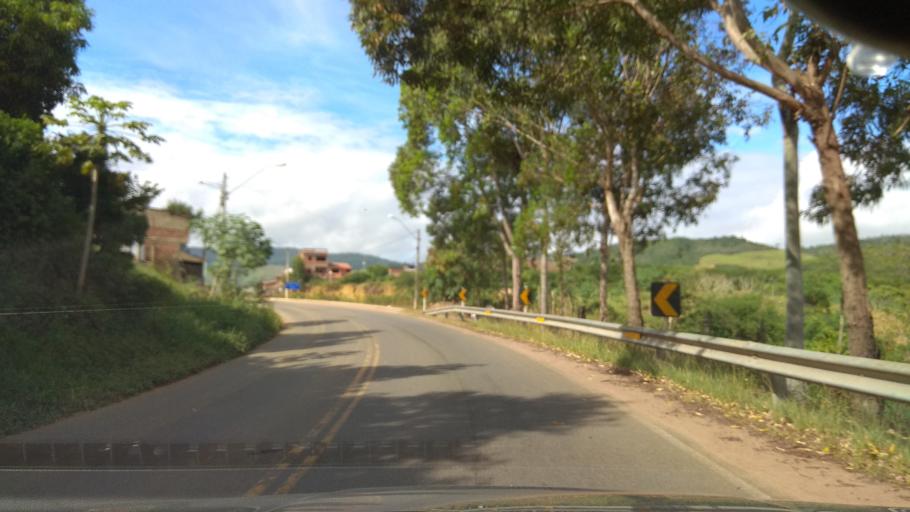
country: BR
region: Bahia
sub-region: Ubaira
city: Ubaira
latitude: -13.2604
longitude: -39.6651
